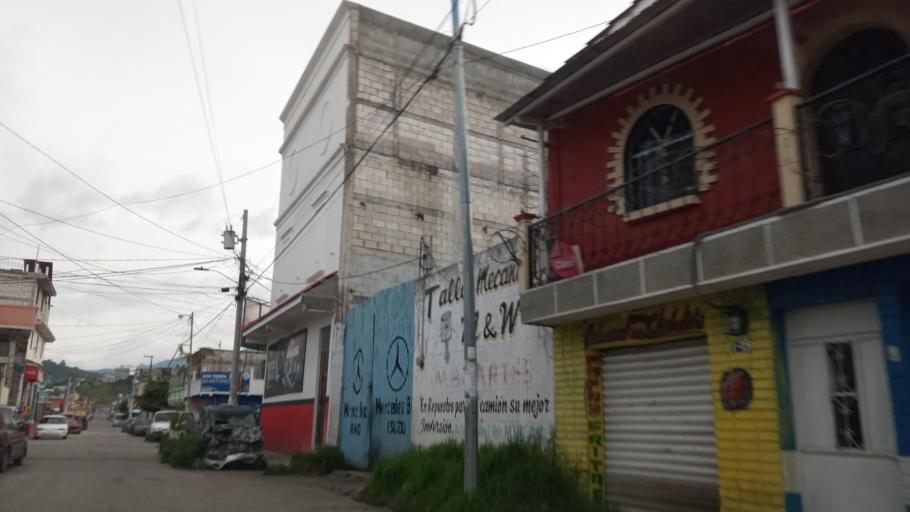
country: GT
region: Quetzaltenango
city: Quetzaltenango
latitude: 14.8432
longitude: -91.5072
